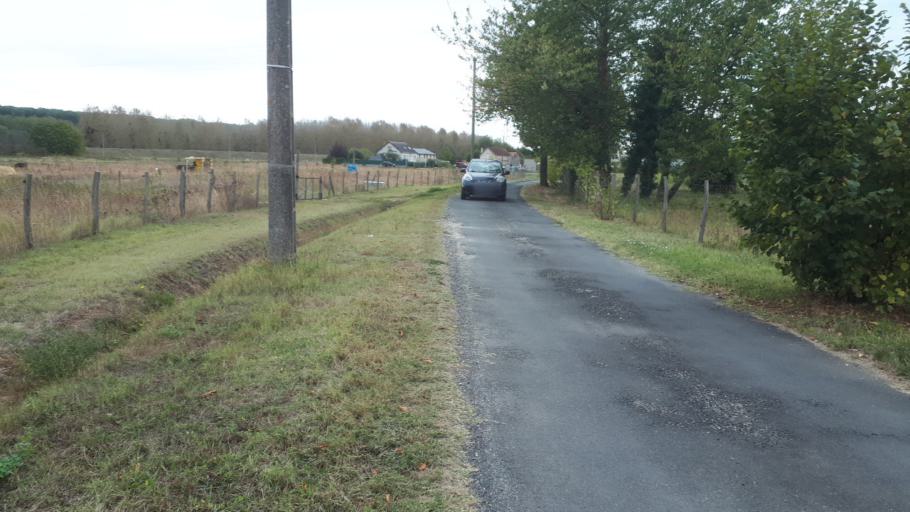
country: FR
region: Centre
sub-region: Departement du Loir-et-Cher
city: Blois
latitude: 47.5717
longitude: 1.3376
